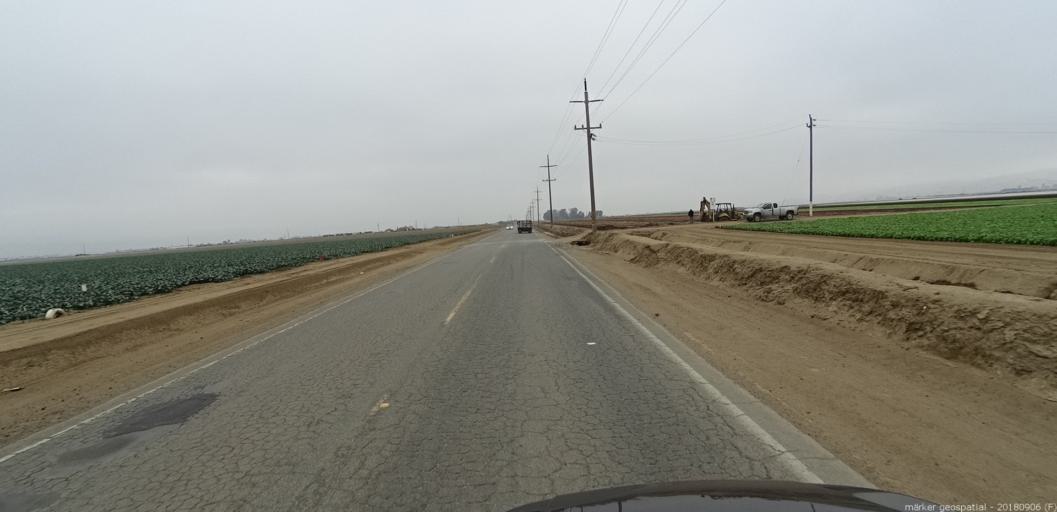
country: US
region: California
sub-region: Monterey County
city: Salinas
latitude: 36.6516
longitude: -121.5822
